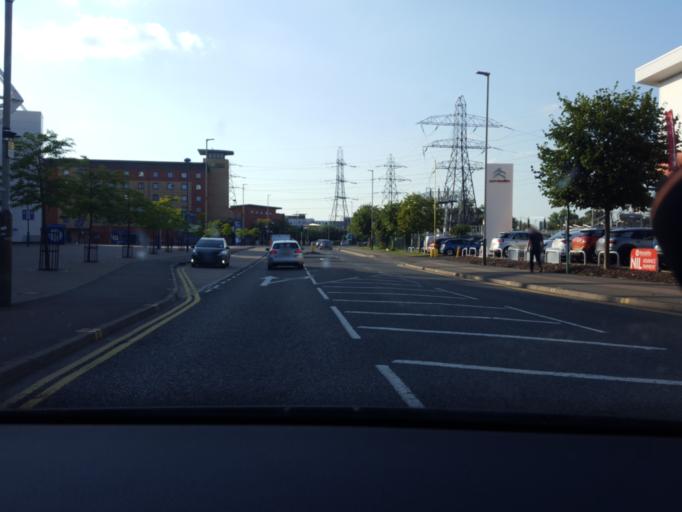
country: GB
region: England
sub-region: City of Leicester
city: Leicester
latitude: 52.6209
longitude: -1.1404
